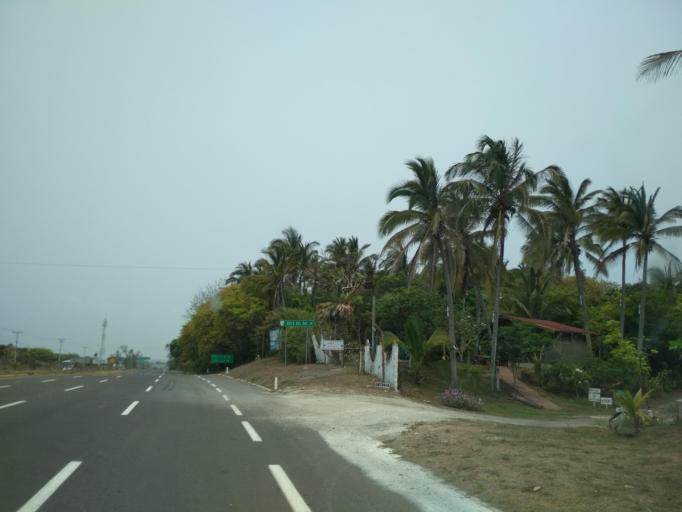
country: MX
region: Veracruz
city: Anton Lizardo
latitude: 19.0515
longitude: -96.0121
